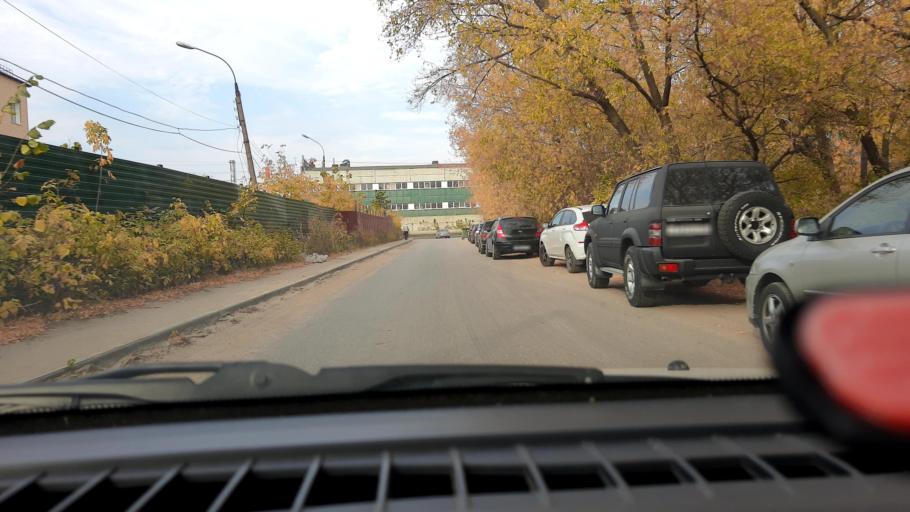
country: RU
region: Nizjnij Novgorod
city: Nizhniy Novgorod
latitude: 56.2675
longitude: 43.9464
